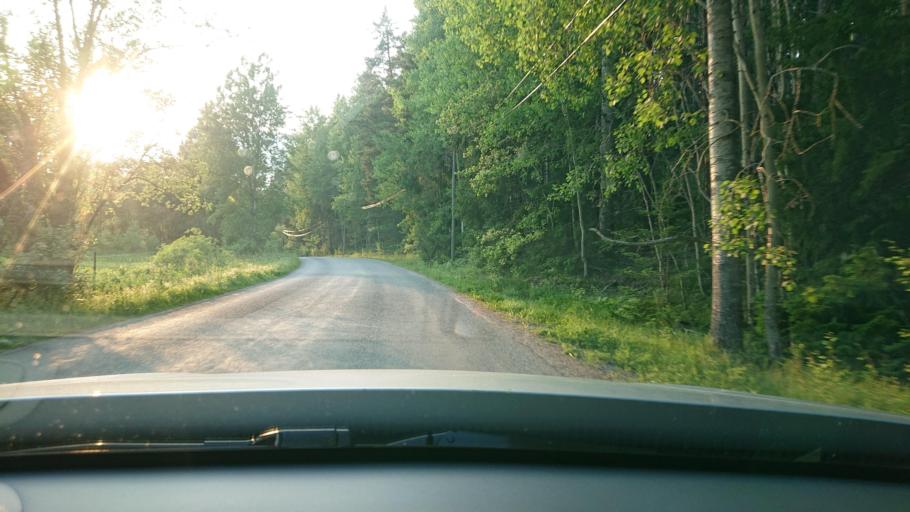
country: SE
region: Stockholm
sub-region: Osterakers Kommun
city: Akersberga
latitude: 59.5025
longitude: 18.3421
